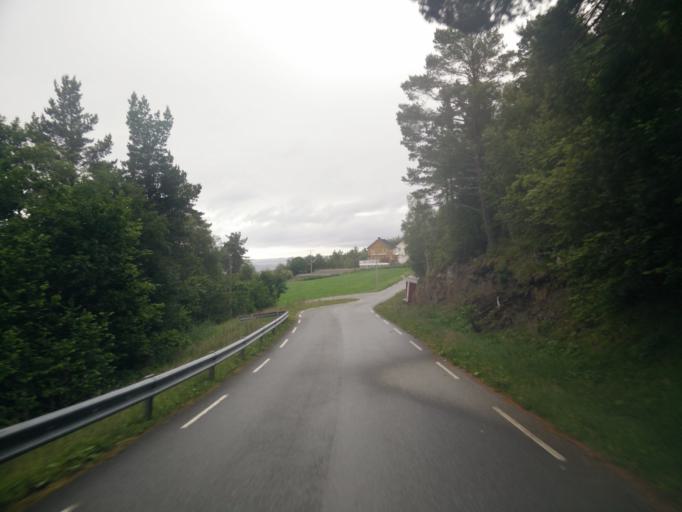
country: NO
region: More og Romsdal
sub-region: Kristiansund
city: Rensvik
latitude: 63.0336
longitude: 7.9126
